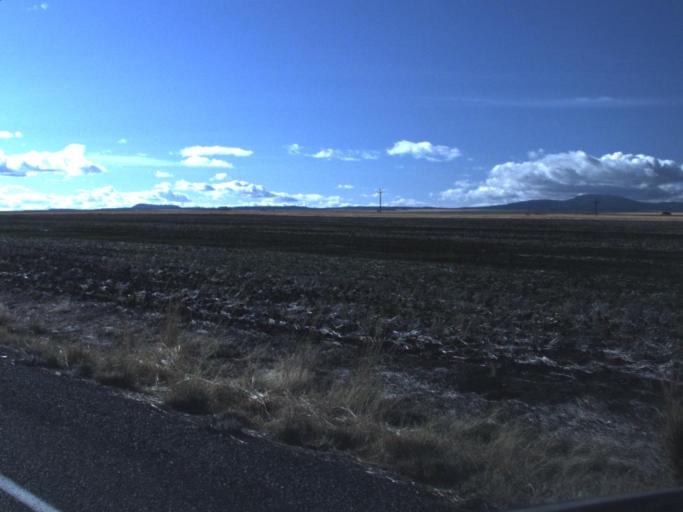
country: US
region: Washington
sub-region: Asotin County
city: Asotin
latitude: 46.2109
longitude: -117.0703
